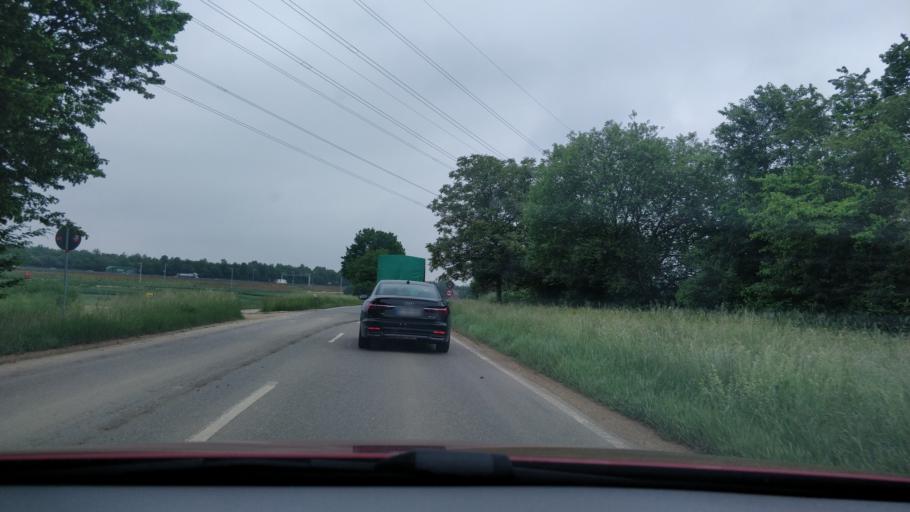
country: DE
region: Baden-Wuerttemberg
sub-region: Regierungsbezirk Stuttgart
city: Denkendorf
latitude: 48.6900
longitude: 9.3041
